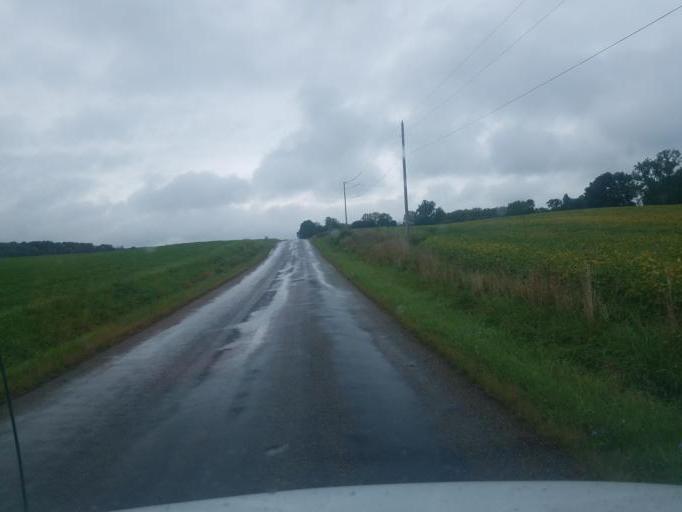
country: US
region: Ohio
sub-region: Wayne County
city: West Salem
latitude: 40.9409
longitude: -82.1238
